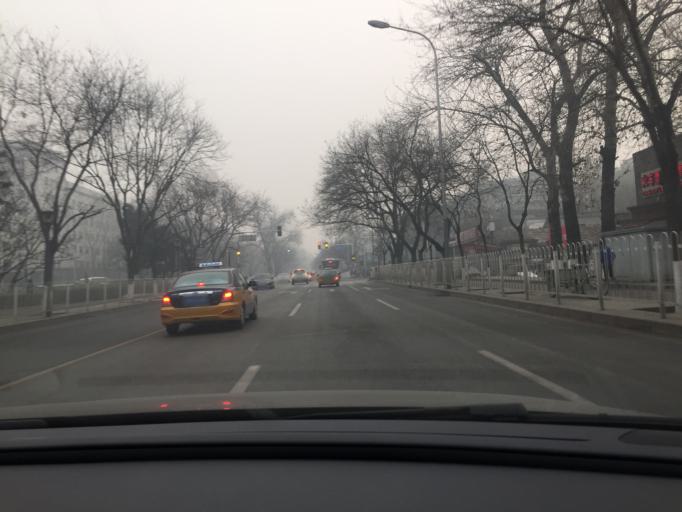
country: CN
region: Beijing
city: Beijing
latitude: 39.9147
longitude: 116.4003
